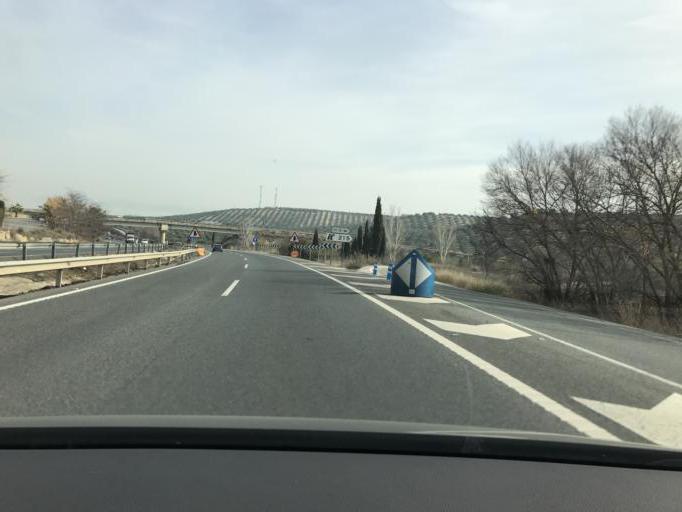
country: ES
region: Andalusia
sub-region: Provincia de Granada
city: Moraleda de Zafayona
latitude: 37.1784
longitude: -3.9037
